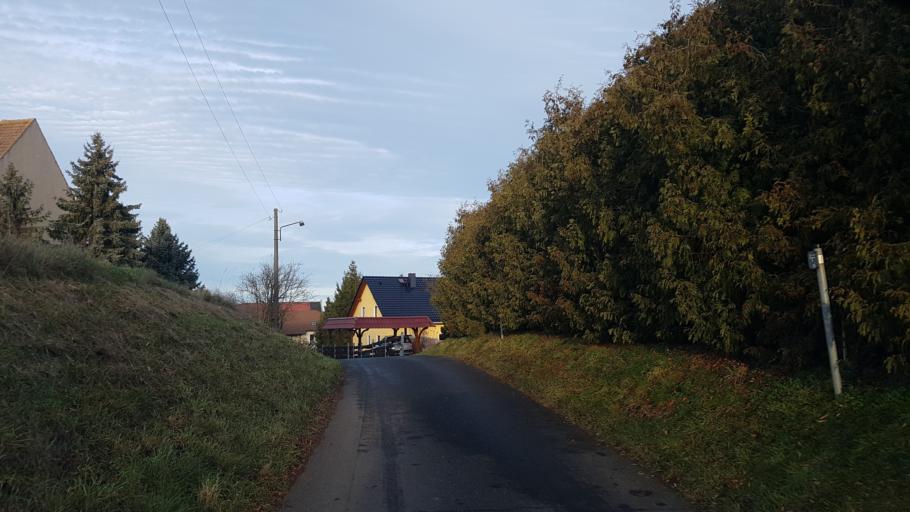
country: DE
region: Saxony
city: Ostrau
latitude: 51.1668
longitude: 13.1593
